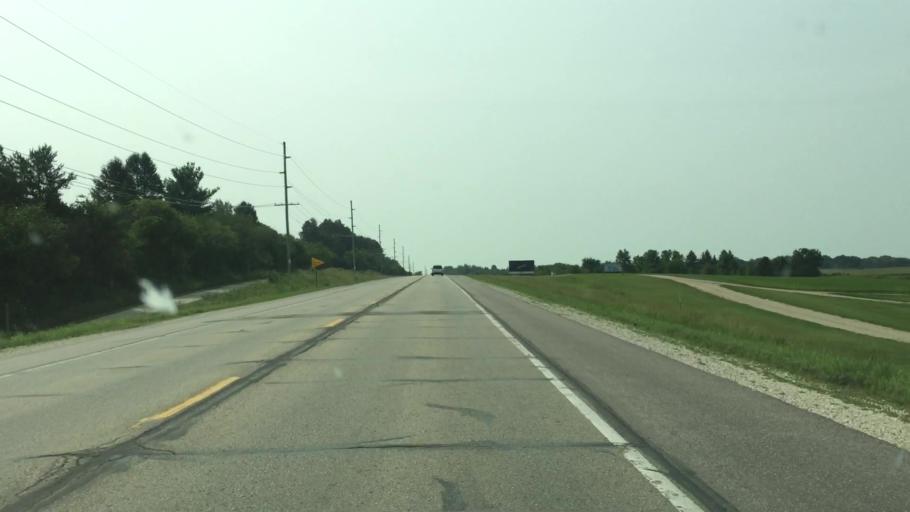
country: US
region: Iowa
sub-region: Dickinson County
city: Milford
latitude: 43.3530
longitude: -95.1799
